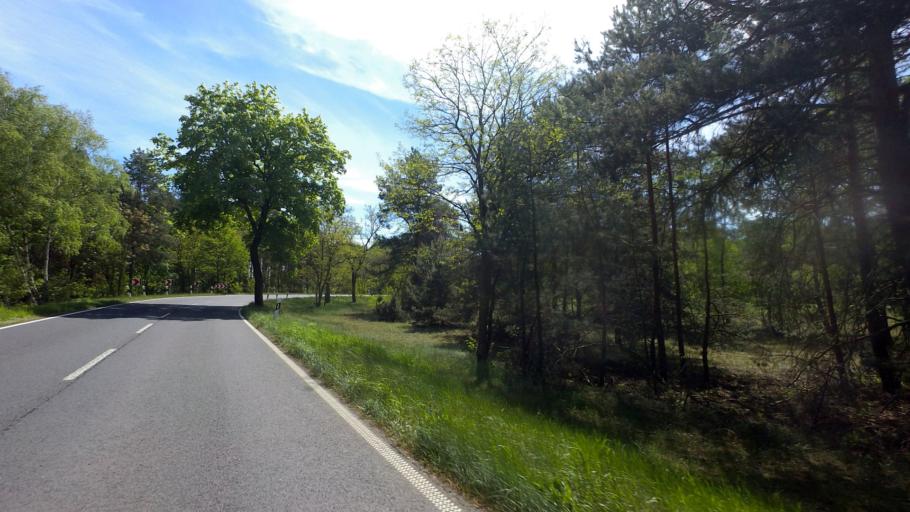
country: DE
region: Brandenburg
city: Luckenwalde
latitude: 52.1351
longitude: 13.1267
